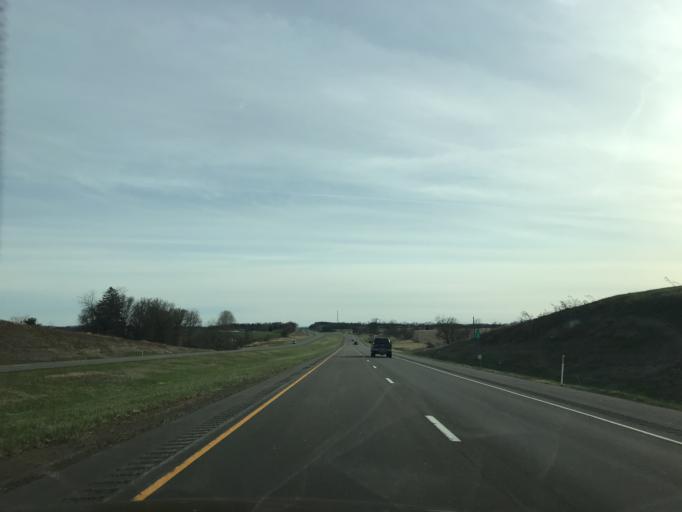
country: US
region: Pennsylvania
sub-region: Northumberland County
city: Watsontown
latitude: 41.0895
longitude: -76.8156
